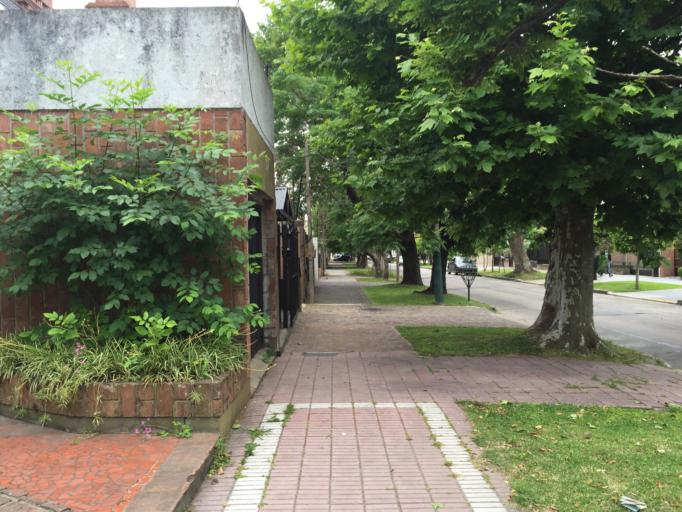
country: AR
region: Buenos Aires
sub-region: Partido de Lomas de Zamora
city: Lomas de Zamora
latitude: -34.7542
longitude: -58.3923
